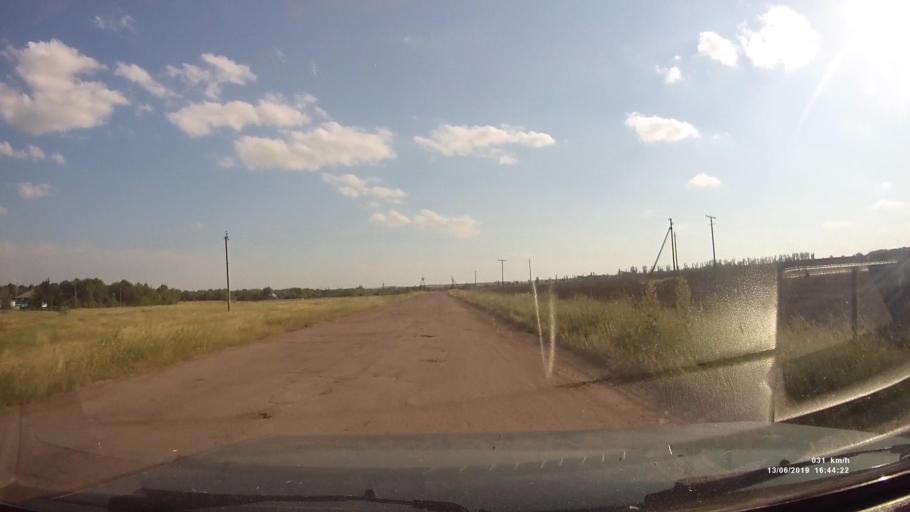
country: RU
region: Rostov
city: Kazanskaya
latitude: 49.9460
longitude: 41.4210
